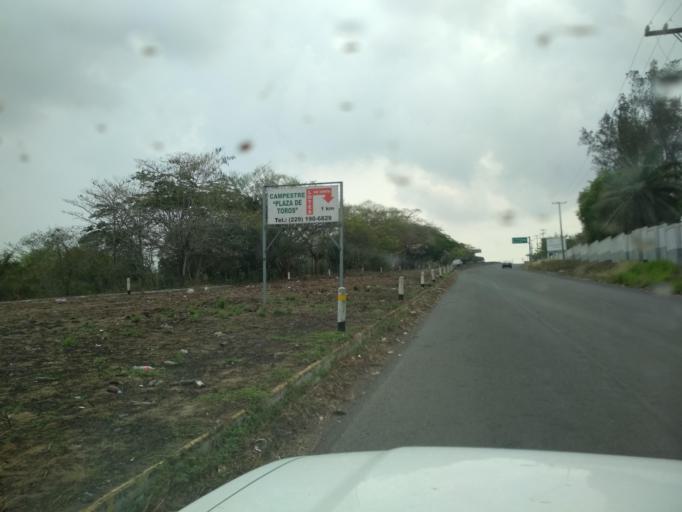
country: MX
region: Veracruz
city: Paso del Toro
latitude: 19.0169
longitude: -96.1392
